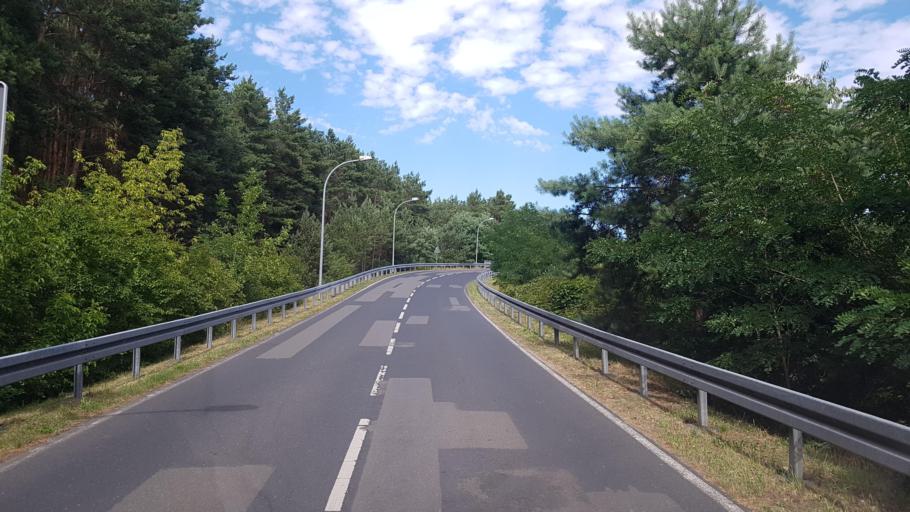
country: DE
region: Brandenburg
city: Luckenwalde
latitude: 52.1173
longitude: 13.1949
